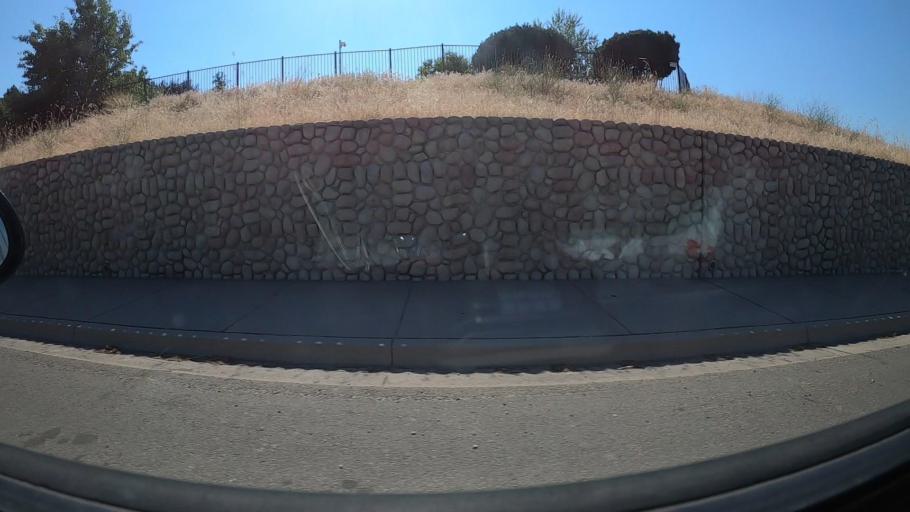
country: US
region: Idaho
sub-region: Ada County
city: Eagle
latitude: 43.6658
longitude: -116.3545
